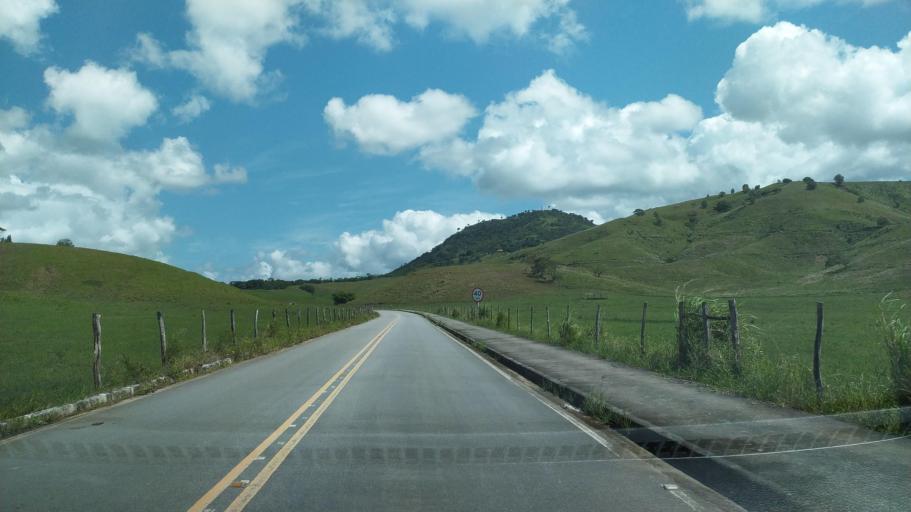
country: BR
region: Alagoas
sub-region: Uniao Dos Palmares
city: Uniao dos Palmares
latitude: -9.1632
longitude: -36.0523
